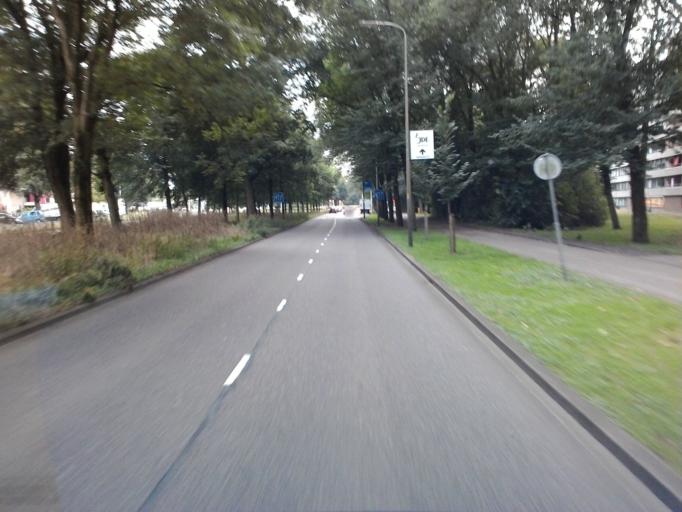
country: NL
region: Utrecht
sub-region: Gemeente Utrecht
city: Utrecht
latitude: 52.1179
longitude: 5.1112
